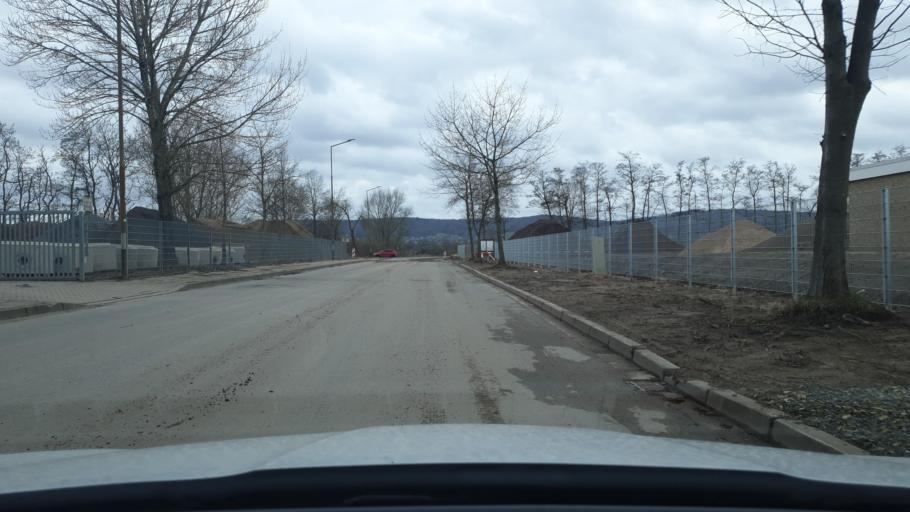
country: DE
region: North Rhine-Westphalia
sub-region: Regierungsbezirk Detmold
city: Hille
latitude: 52.3220
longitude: 8.7470
